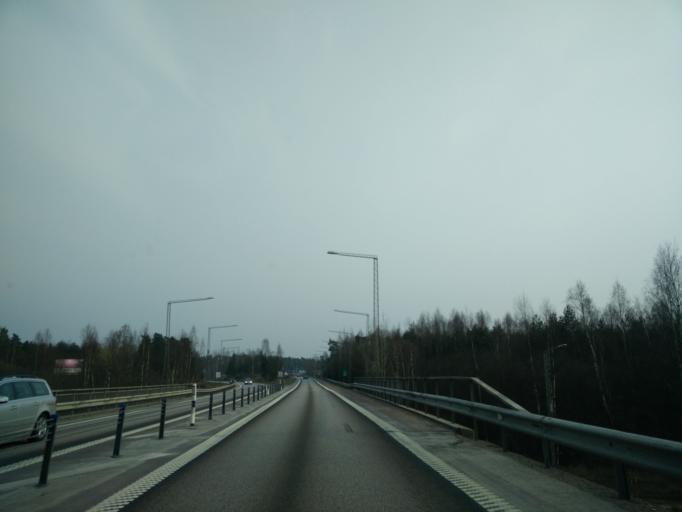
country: SE
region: Vaermland
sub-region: Hammaro Kommun
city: Skoghall
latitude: 59.3824
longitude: 13.4252
